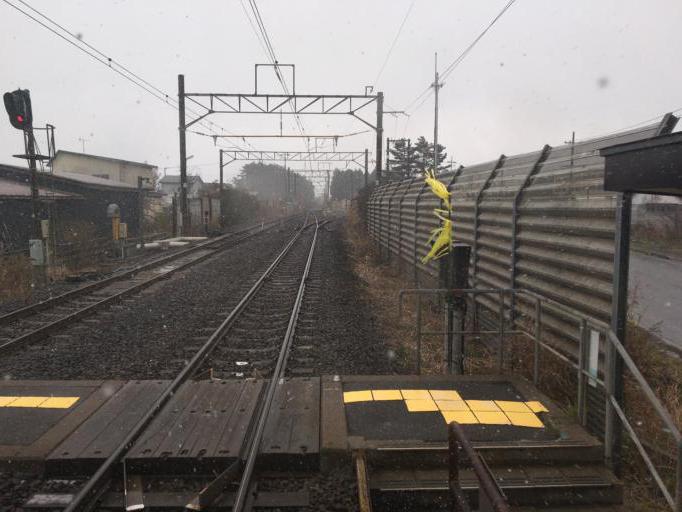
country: JP
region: Aomori
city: Aomori Shi
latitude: 40.9877
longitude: 140.6524
